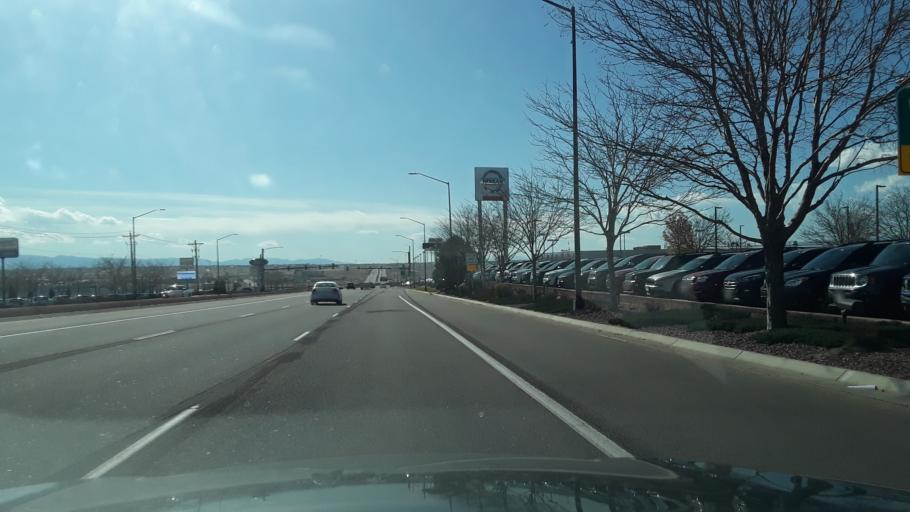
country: US
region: Colorado
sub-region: Pueblo County
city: Pueblo
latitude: 38.3111
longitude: -104.6393
